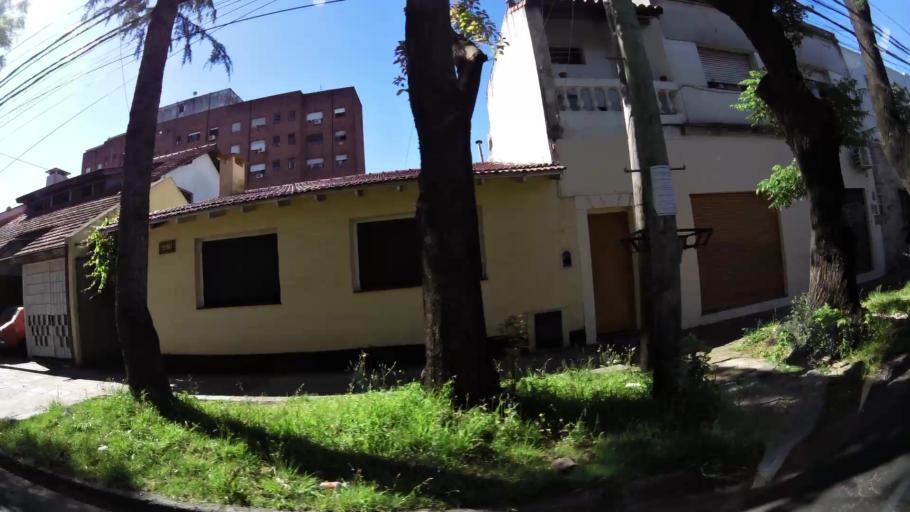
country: AR
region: Buenos Aires
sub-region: Partido de Vicente Lopez
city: Olivos
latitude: -34.5346
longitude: -58.5132
